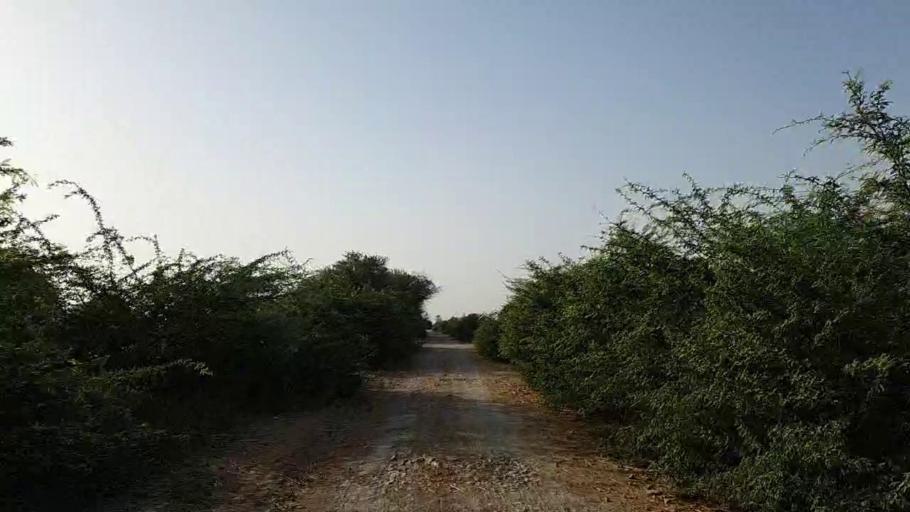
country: PK
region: Sindh
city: Jati
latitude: 24.3408
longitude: 68.1482
